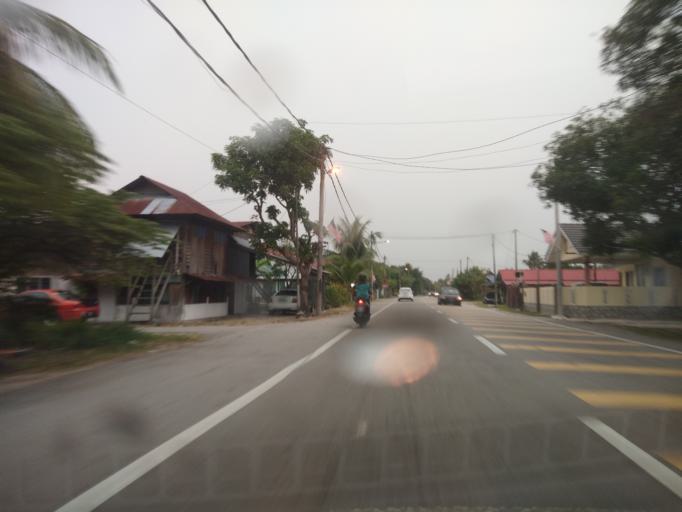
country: MY
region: Penang
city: Permatang Kuching
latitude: 5.4893
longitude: 100.3998
